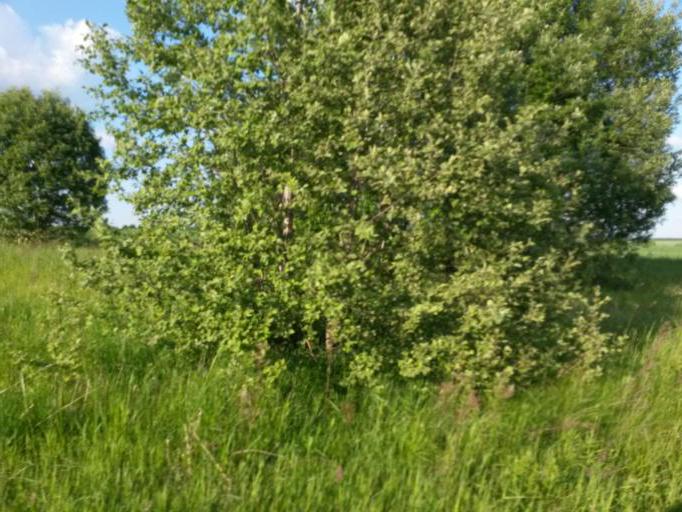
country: RU
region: Jaroslavl
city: Burmakino
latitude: 57.3581
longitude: 40.2014
